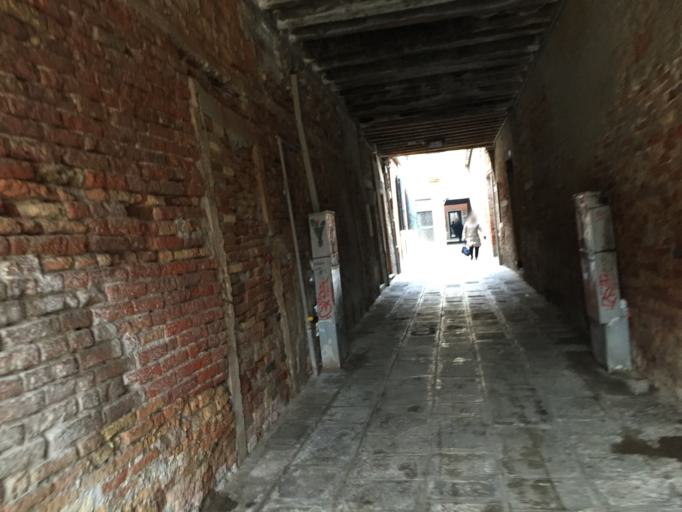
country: IT
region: Veneto
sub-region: Provincia di Venezia
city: Venice
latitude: 45.4449
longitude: 12.3230
